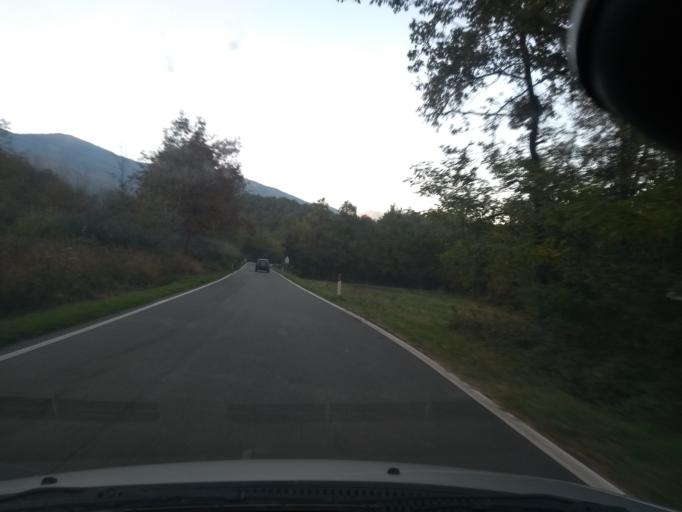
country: IT
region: Piedmont
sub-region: Provincia di Torino
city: La Cassa
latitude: 45.1985
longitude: 7.5150
